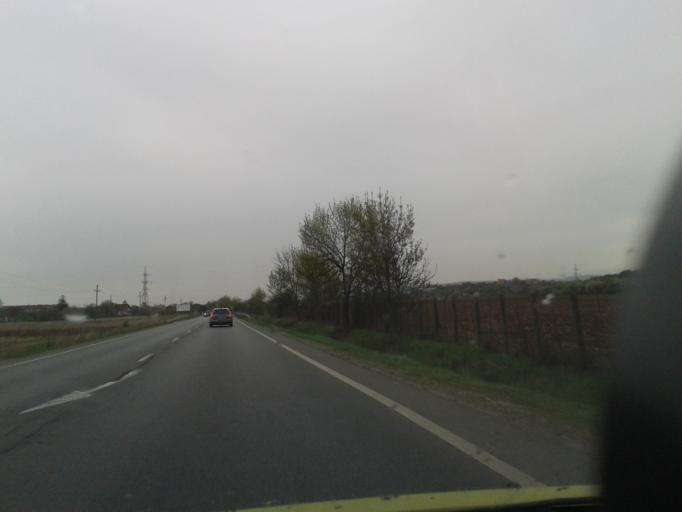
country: RO
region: Hunedoara
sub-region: Oras Simeria
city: Simeria
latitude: 45.8484
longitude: 22.9951
